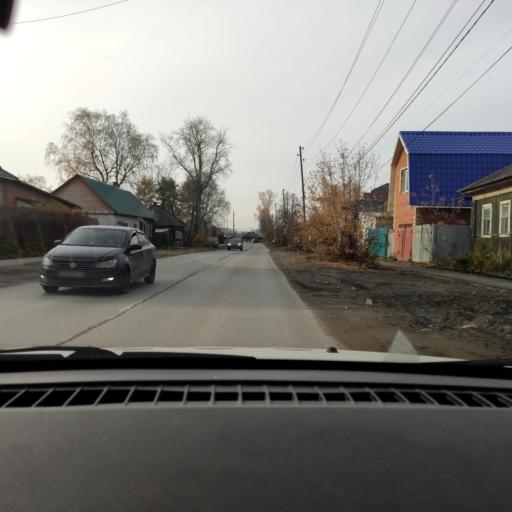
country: RU
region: Perm
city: Perm
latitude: 58.0448
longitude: 56.3289
